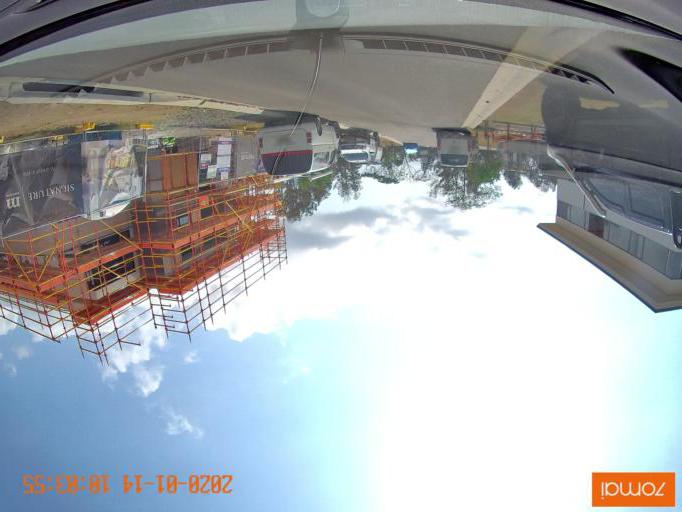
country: AU
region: New South Wales
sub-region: Wyong Shire
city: Kingfisher Shores
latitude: -33.1259
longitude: 151.5372
